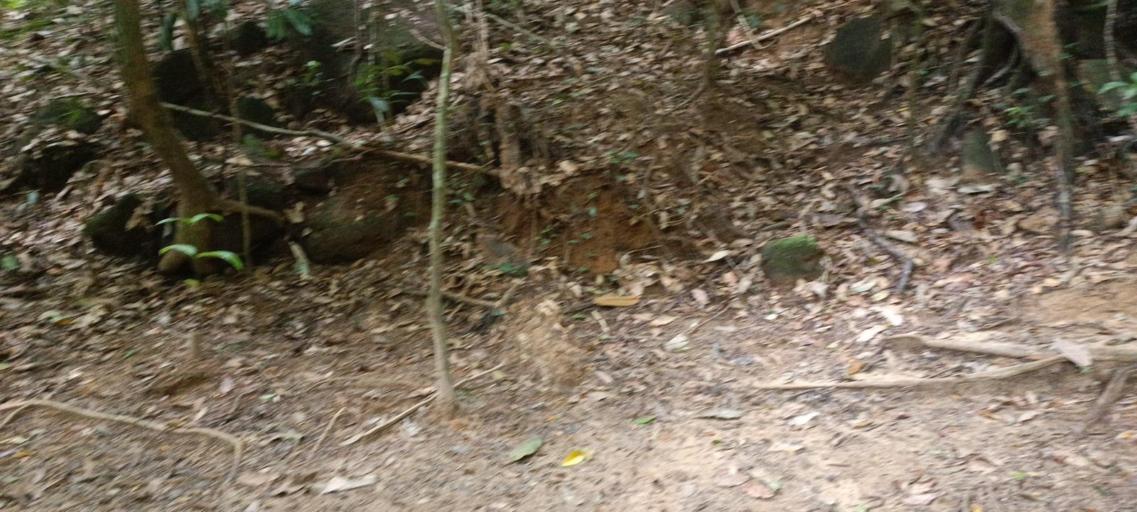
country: MY
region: Penang
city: Bukit Mertajam
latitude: 5.3631
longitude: 100.4844
